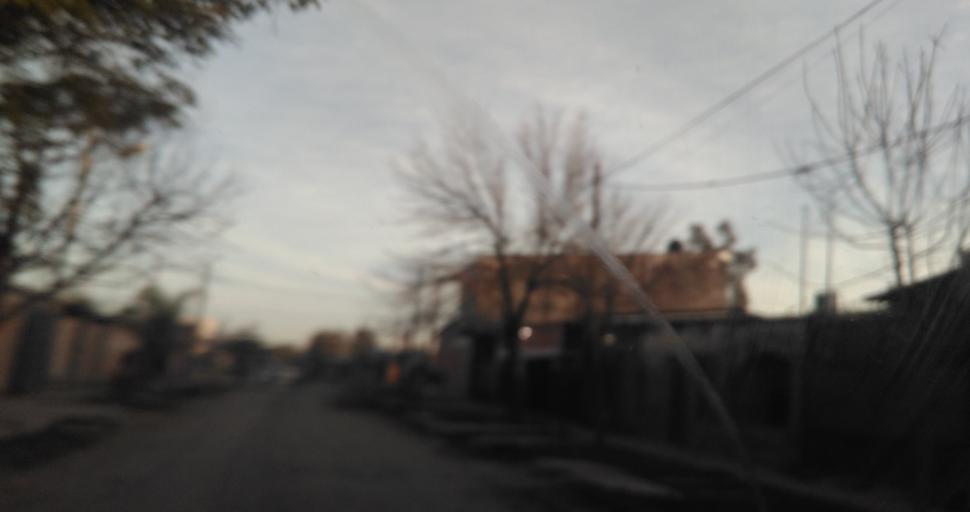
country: AR
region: Chaco
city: Resistencia
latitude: -27.4654
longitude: -59.0100
